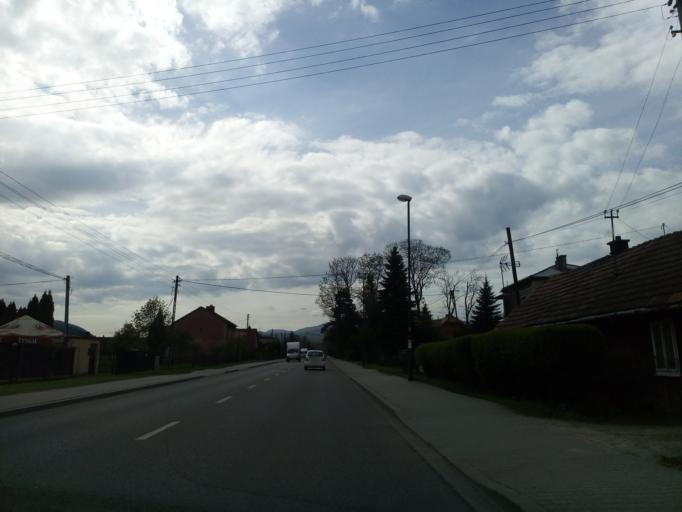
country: PL
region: Lesser Poland Voivodeship
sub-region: Powiat nowosadecki
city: Nawojowa
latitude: 49.5761
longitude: 20.7319
